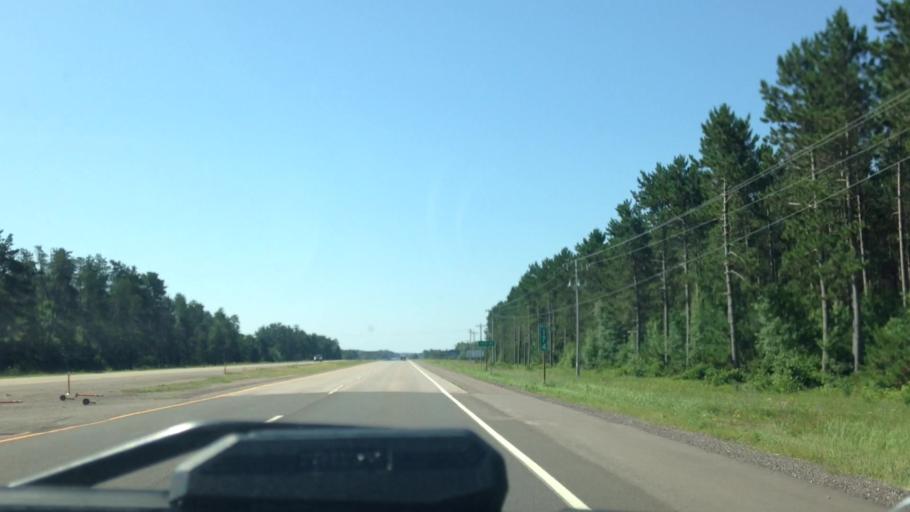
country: US
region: Wisconsin
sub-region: Washburn County
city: Spooner
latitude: 45.9246
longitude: -91.8278
